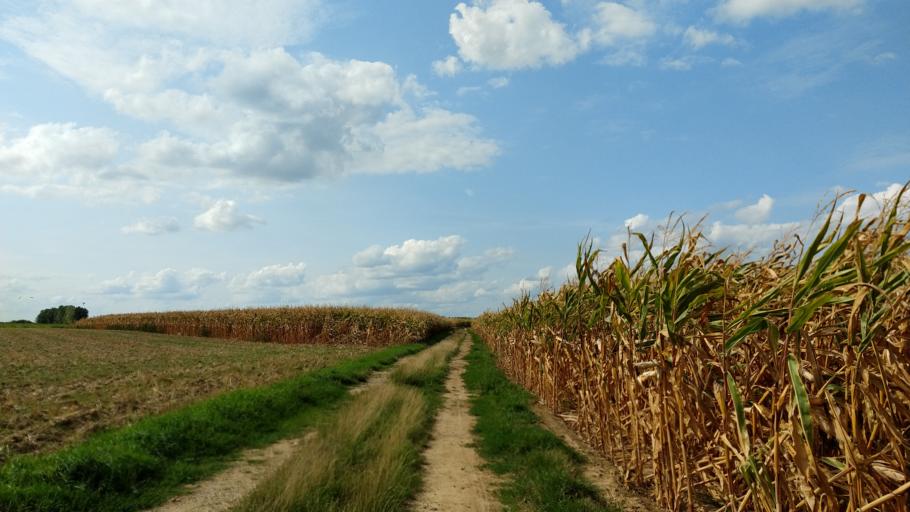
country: BE
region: Flanders
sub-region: Provincie Vlaams-Brabant
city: Boutersem
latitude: 50.8218
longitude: 4.8600
